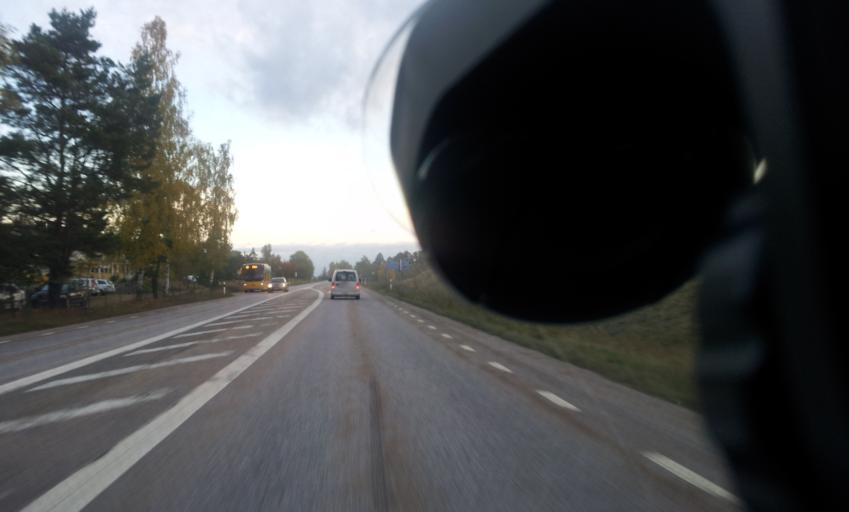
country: SE
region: Kalmar
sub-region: Vasterviks Kommun
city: Ankarsrum
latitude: 57.7083
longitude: 16.4471
